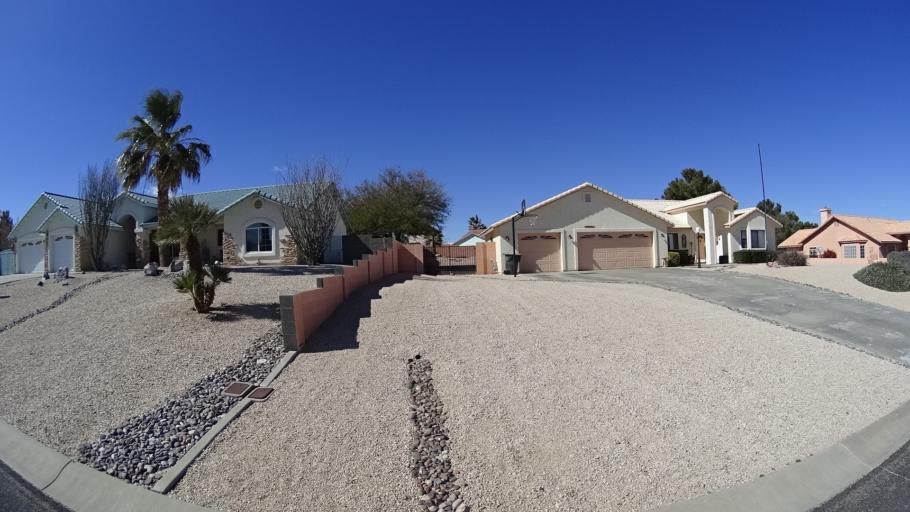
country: US
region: Arizona
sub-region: Mohave County
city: Kingman
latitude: 35.2019
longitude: -113.9620
